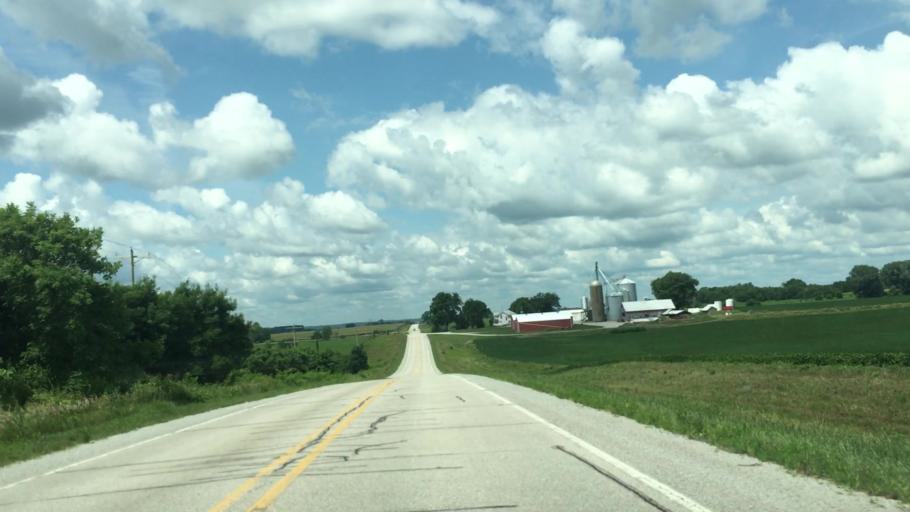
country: US
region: Iowa
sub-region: Johnson County
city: Solon
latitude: 41.8312
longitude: -91.4874
